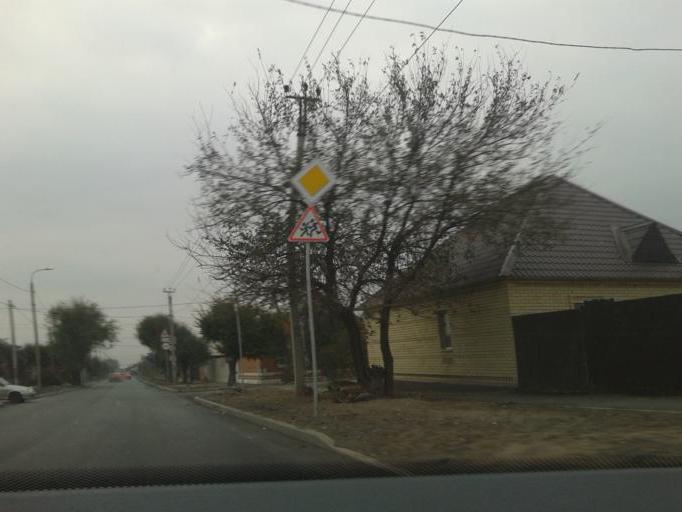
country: RU
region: Volgograd
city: Volgograd
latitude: 48.6999
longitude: 44.4639
